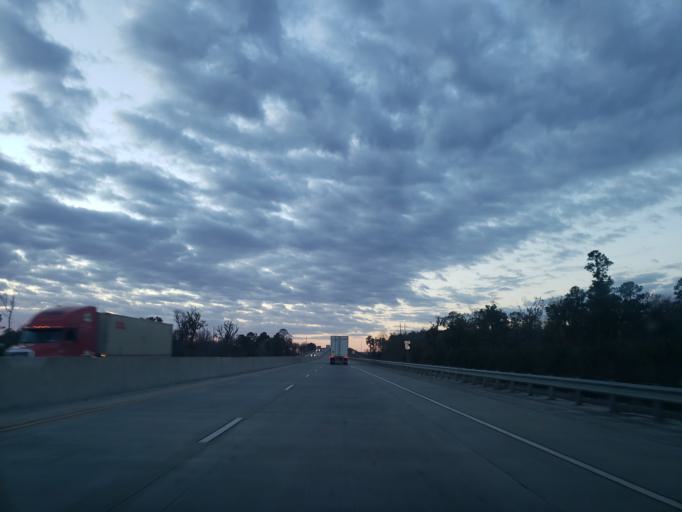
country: US
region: Georgia
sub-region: Chatham County
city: Port Wentworth
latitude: 32.1591
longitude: -81.1772
